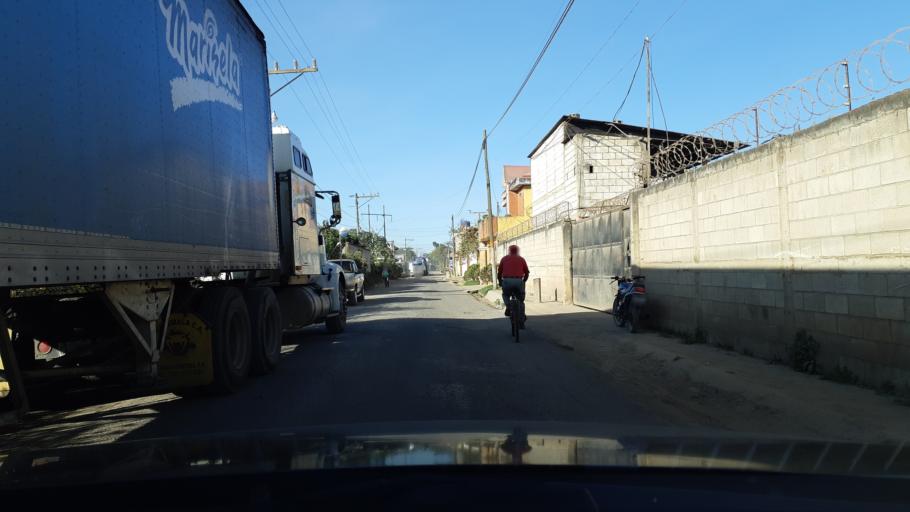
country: GT
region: Chimaltenango
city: El Tejar
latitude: 14.6428
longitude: -90.7990
